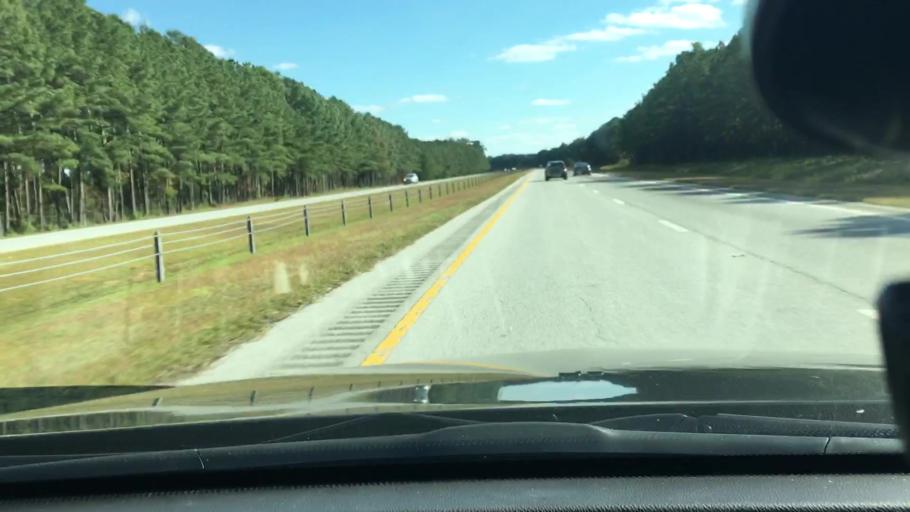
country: US
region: North Carolina
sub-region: Pitt County
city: Farmville
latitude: 35.6318
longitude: -77.7191
